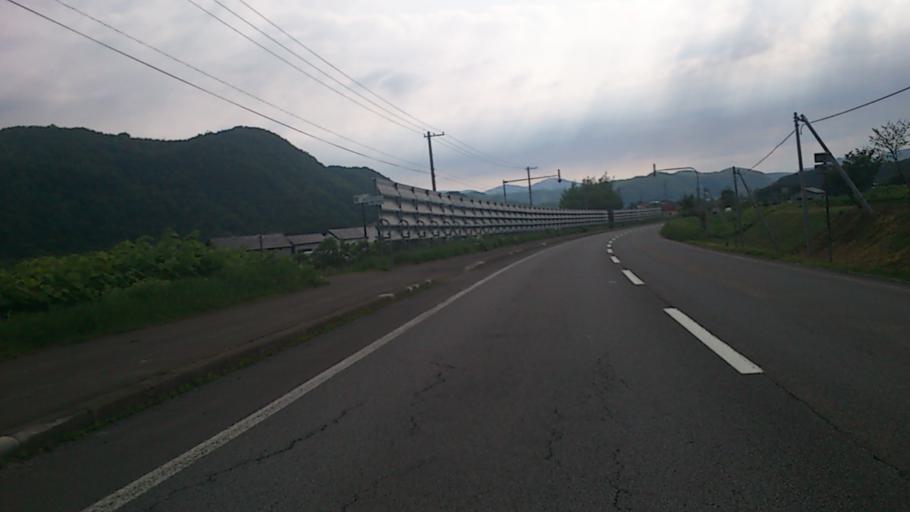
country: JP
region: Hokkaido
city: Kamikawa
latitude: 43.8430
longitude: 142.7145
